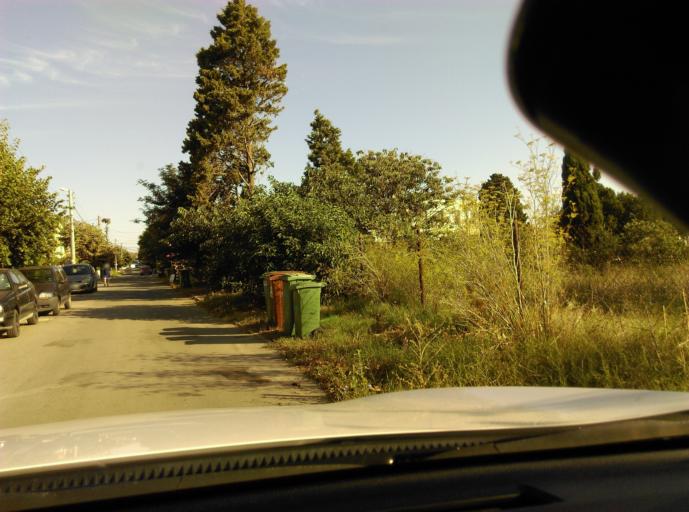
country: BG
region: Burgas
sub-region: Obshtina Kameno
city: Kameno
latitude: 42.5999
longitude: 27.3840
